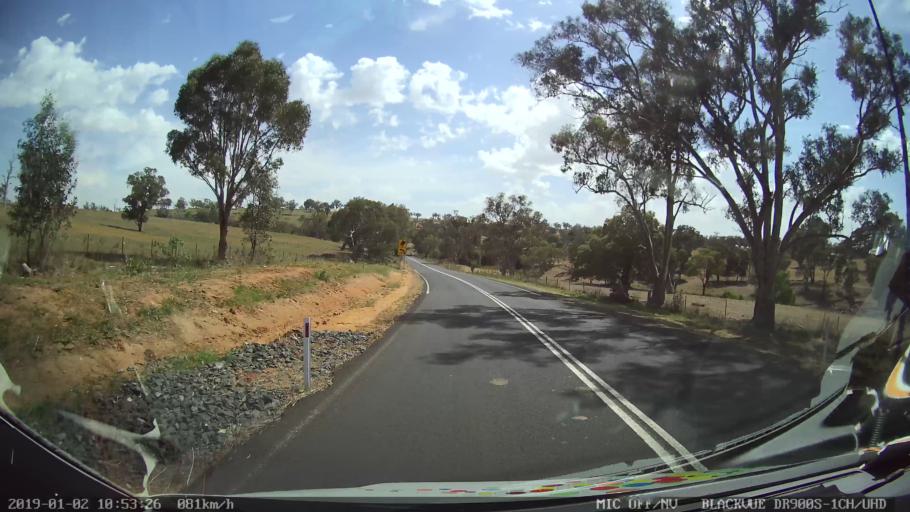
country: AU
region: New South Wales
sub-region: Cootamundra
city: Cootamundra
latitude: -34.6784
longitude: 148.2761
